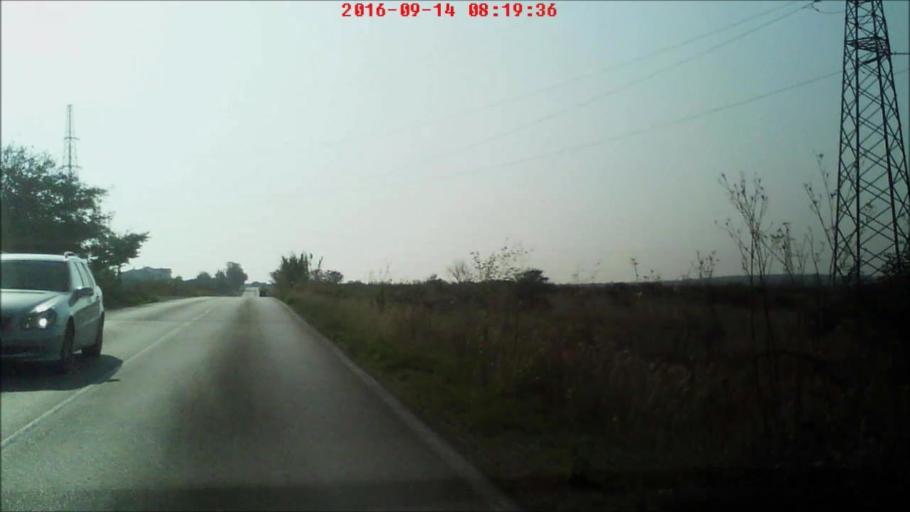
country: HR
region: Zadarska
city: Nin
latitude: 44.2315
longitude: 15.1919
